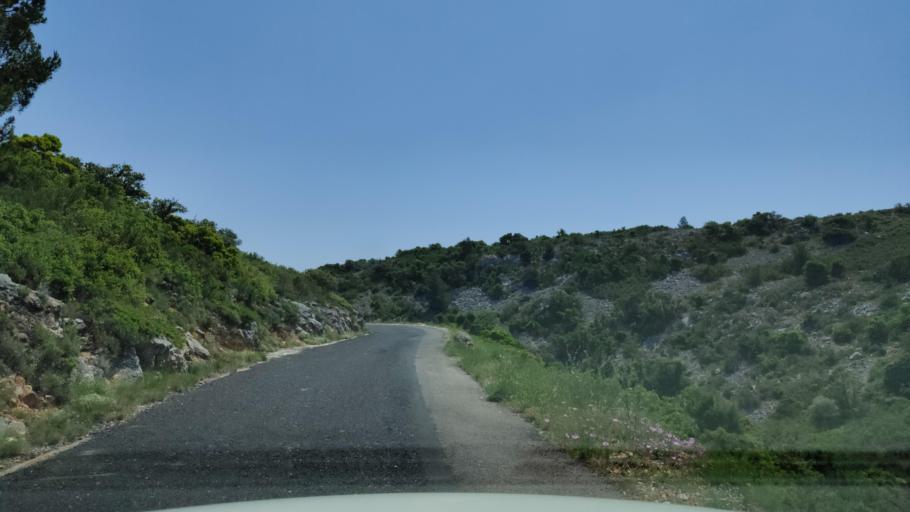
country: FR
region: Languedoc-Roussillon
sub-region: Departement des Pyrenees-Orientales
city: Estagel
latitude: 42.7860
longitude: 2.7447
